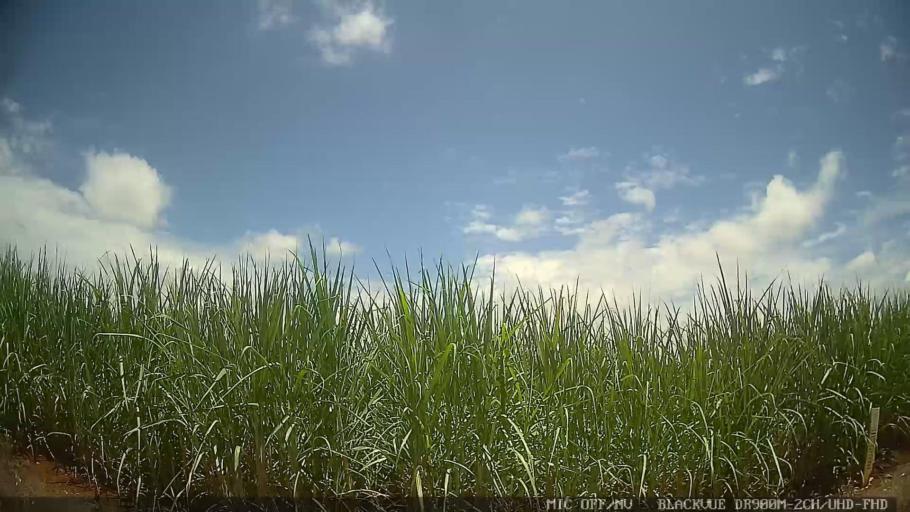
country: BR
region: Sao Paulo
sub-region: Laranjal Paulista
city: Laranjal Paulista
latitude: -23.0310
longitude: -47.8583
